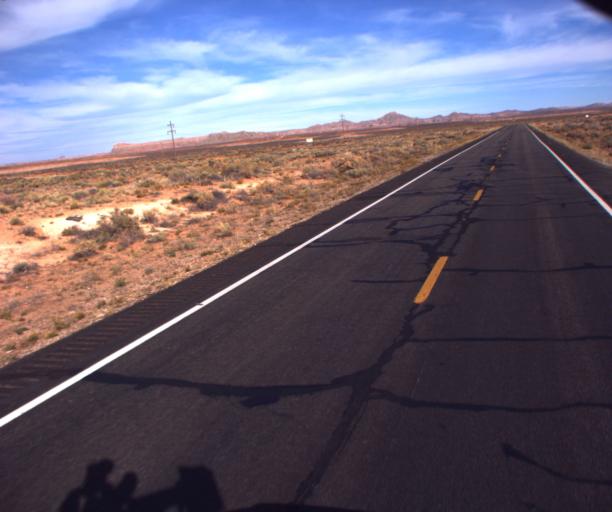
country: US
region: Arizona
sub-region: Apache County
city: Many Farms
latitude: 36.9414
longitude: -109.6555
